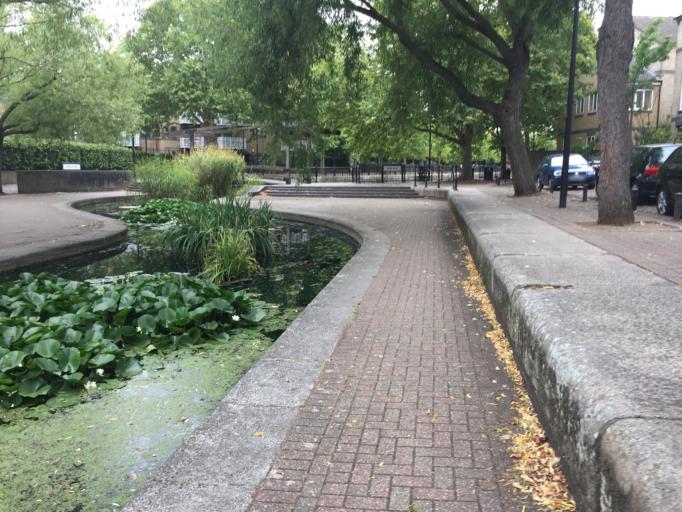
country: GB
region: England
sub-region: Greater London
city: Bethnal Green
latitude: 51.5017
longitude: -0.0460
